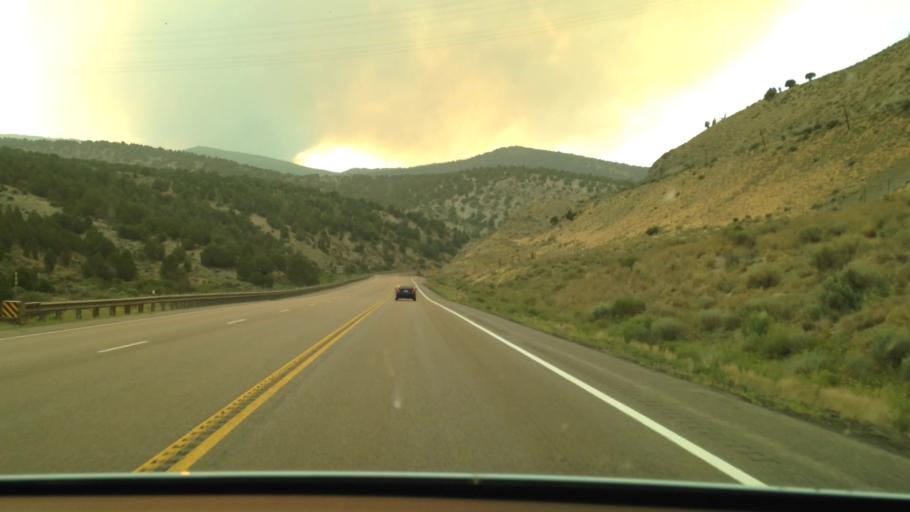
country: US
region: Utah
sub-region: Sanpete County
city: Fairview
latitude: 39.9295
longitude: -111.1916
